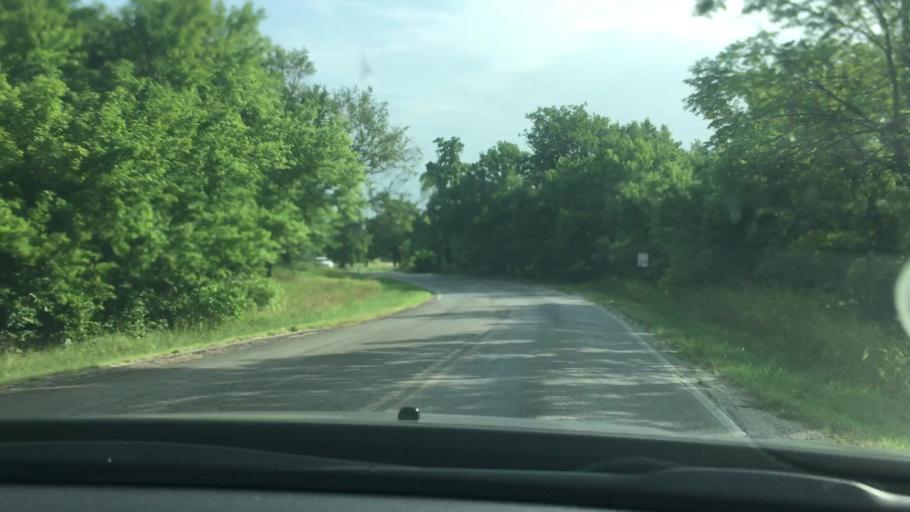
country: US
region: Oklahoma
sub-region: Pontotoc County
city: Byng
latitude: 34.8704
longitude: -96.5965
